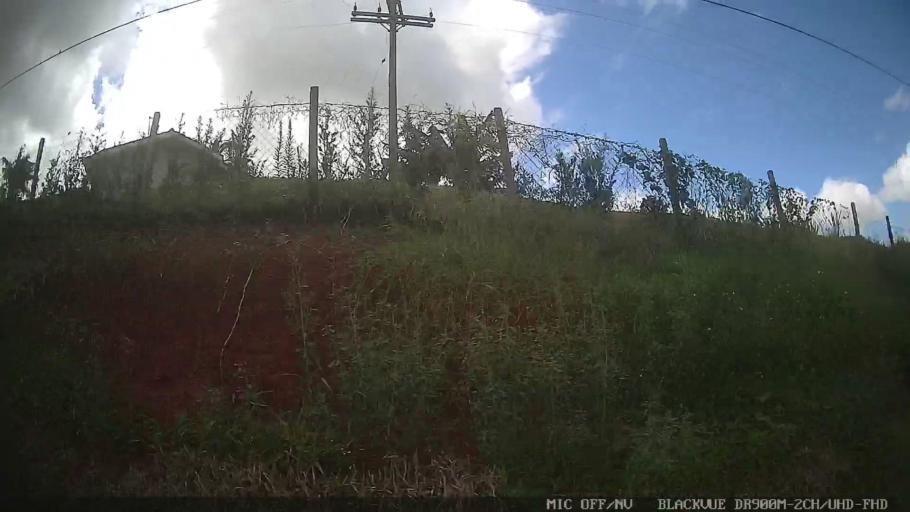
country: BR
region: Sao Paulo
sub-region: Braganca Paulista
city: Braganca Paulista
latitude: -22.8626
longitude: -46.6399
